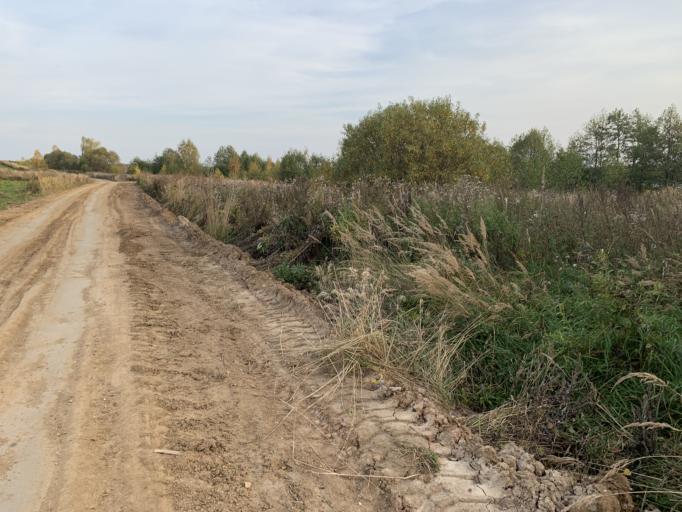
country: RU
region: Jaroslavl
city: Petrovsk
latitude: 56.9799
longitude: 39.3773
